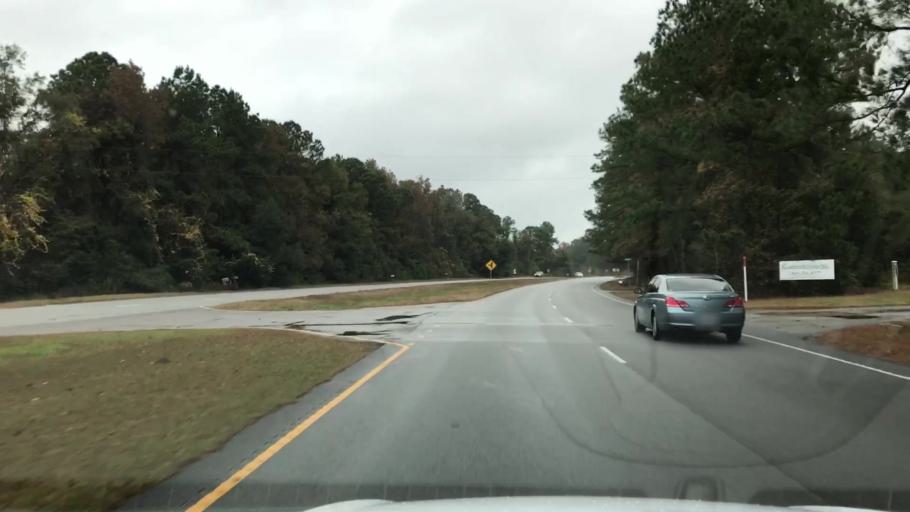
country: US
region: South Carolina
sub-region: Charleston County
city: Awendaw
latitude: 32.9368
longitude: -79.7118
